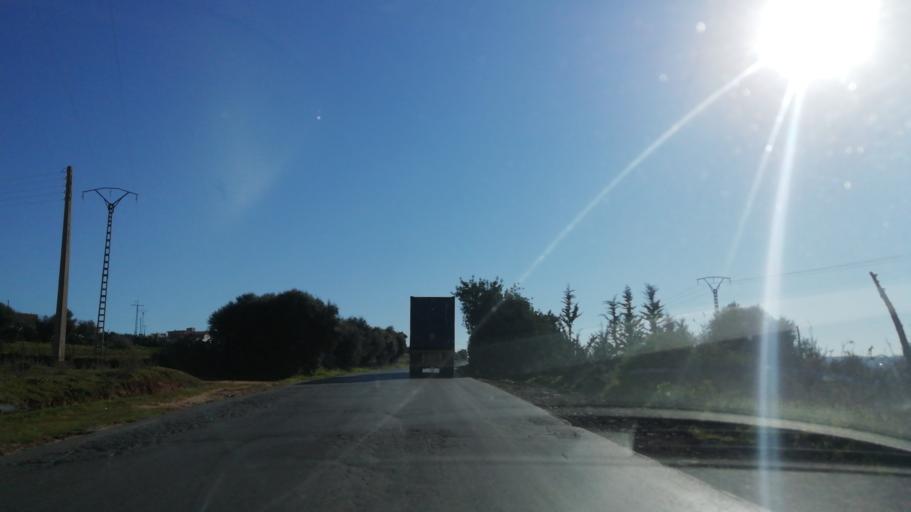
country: DZ
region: Relizane
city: Smala
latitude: 35.6811
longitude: 0.8002
